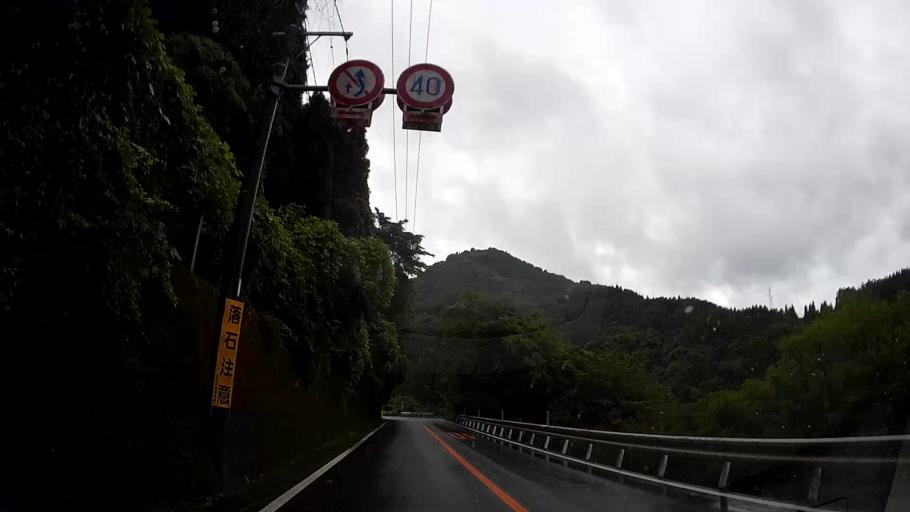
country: JP
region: Oita
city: Hita
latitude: 33.1834
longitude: 130.9982
